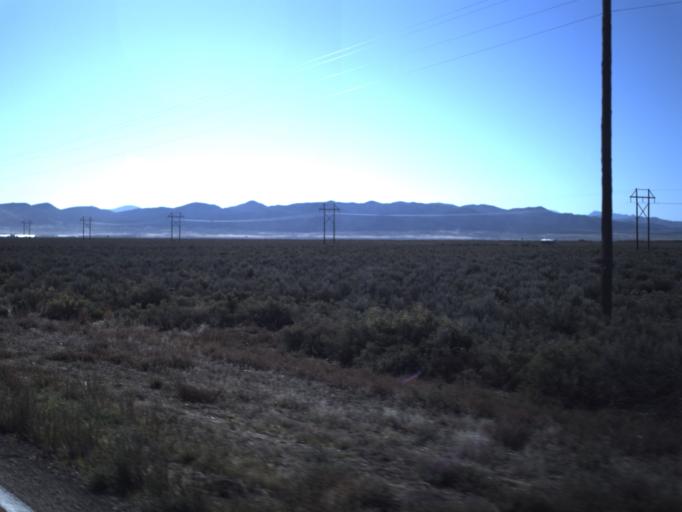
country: US
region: Utah
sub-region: Washington County
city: Enterprise
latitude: 37.7009
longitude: -113.6324
